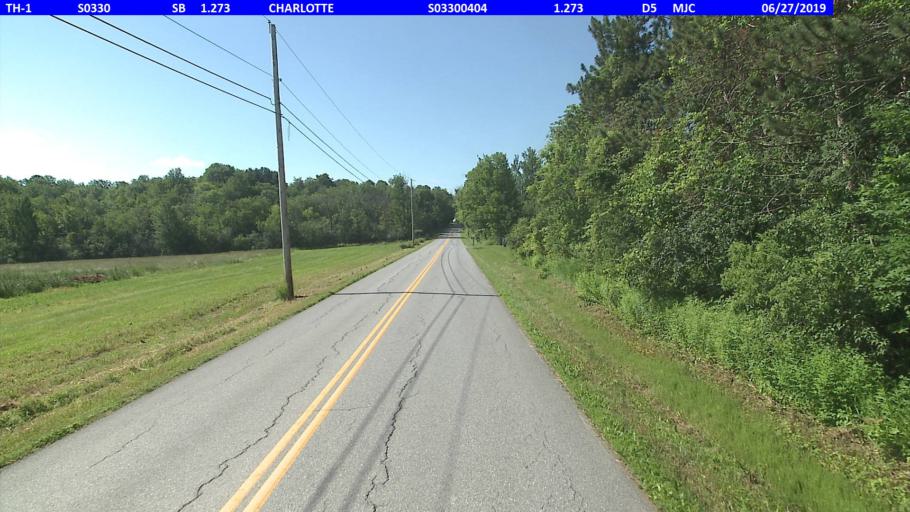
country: US
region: Vermont
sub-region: Chittenden County
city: Hinesburg
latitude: 44.3376
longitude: -73.1933
